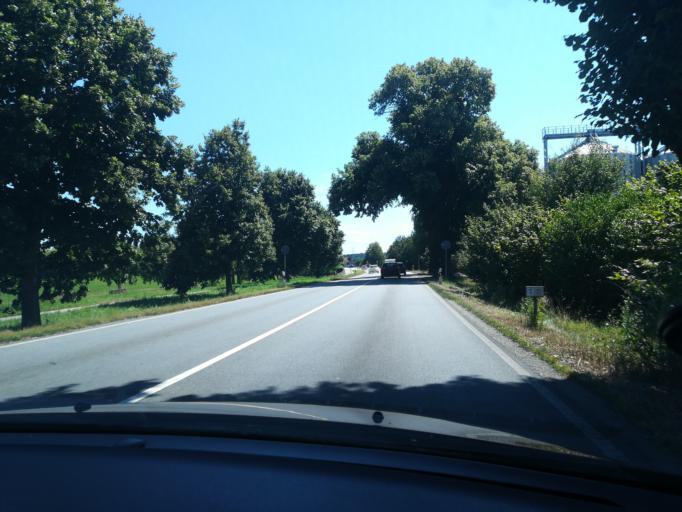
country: DE
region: Bavaria
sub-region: Upper Bavaria
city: Hohenlinden
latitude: 48.1493
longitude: 12.0117
